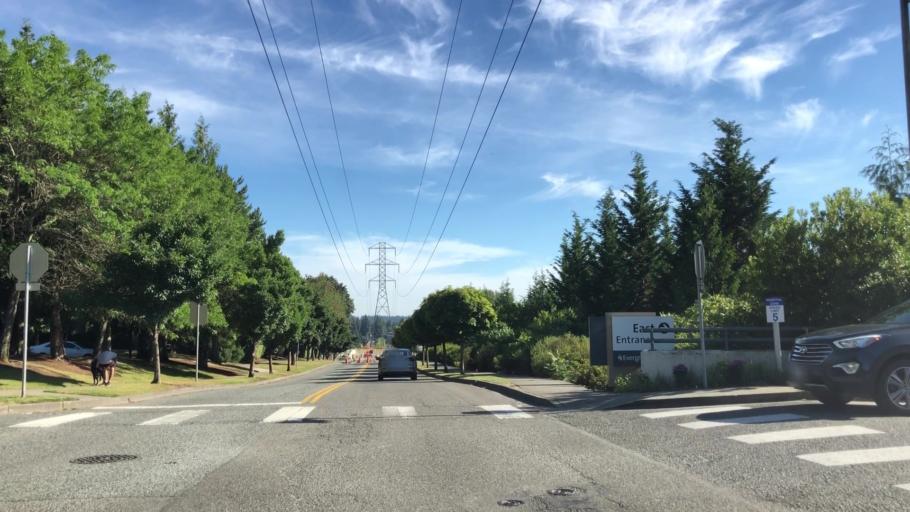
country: US
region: Washington
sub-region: King County
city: Kingsgate
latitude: 47.7158
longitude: -122.1757
